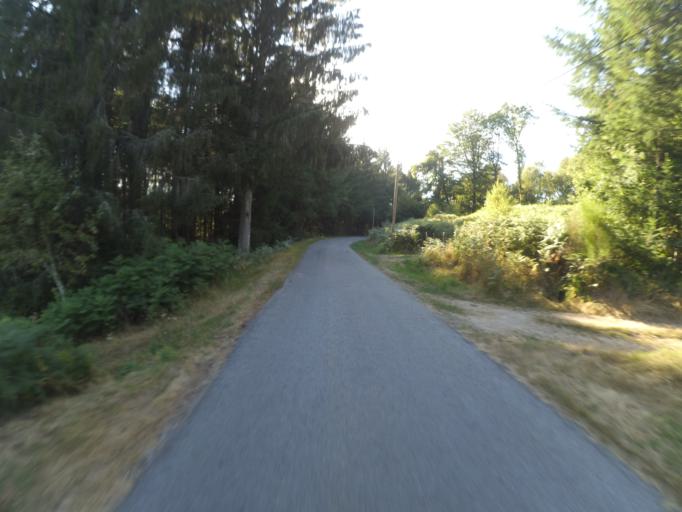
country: FR
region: Limousin
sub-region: Departement de la Creuse
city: Banize
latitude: 45.7601
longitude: 2.0297
